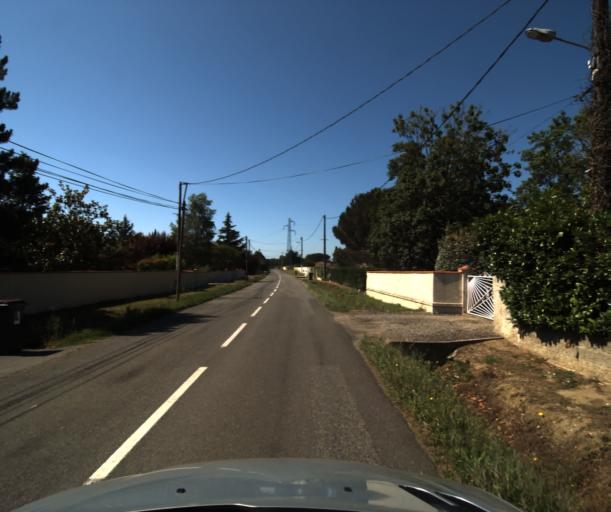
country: FR
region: Midi-Pyrenees
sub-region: Departement de la Haute-Garonne
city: Saubens
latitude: 43.4908
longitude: 1.3521
